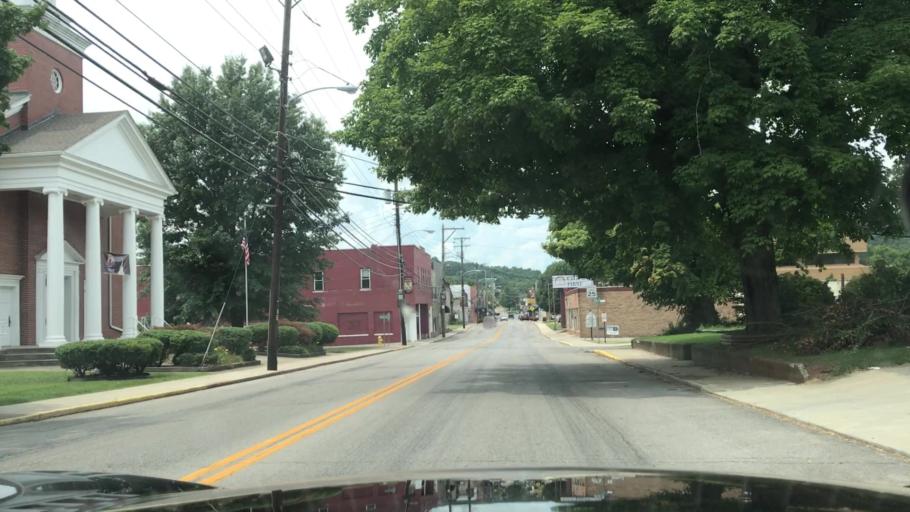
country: US
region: Kentucky
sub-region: Hart County
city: Horse Cave
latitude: 37.1792
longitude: -85.9032
